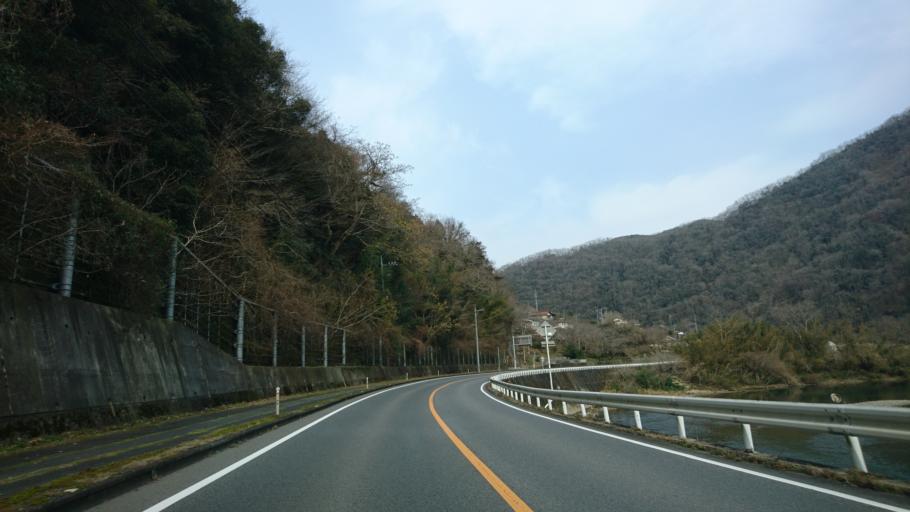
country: JP
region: Okayama
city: Takahashi
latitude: 34.8555
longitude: 133.5692
